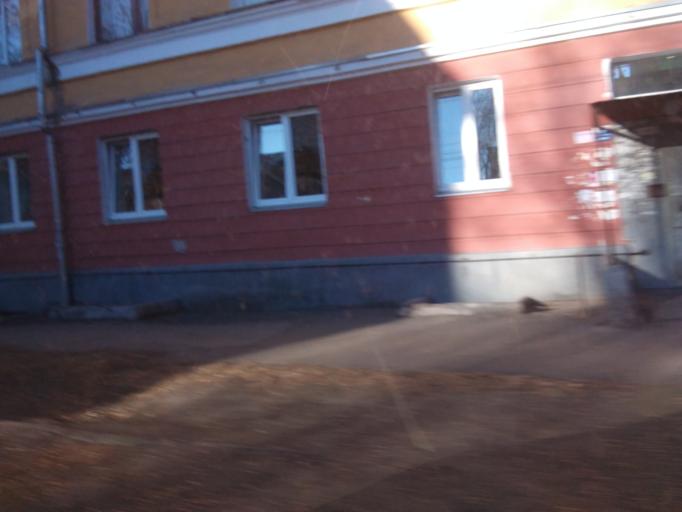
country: RU
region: Chelyabinsk
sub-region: Gorod Magnitogorsk
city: Magnitogorsk
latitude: 53.3886
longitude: 59.0684
